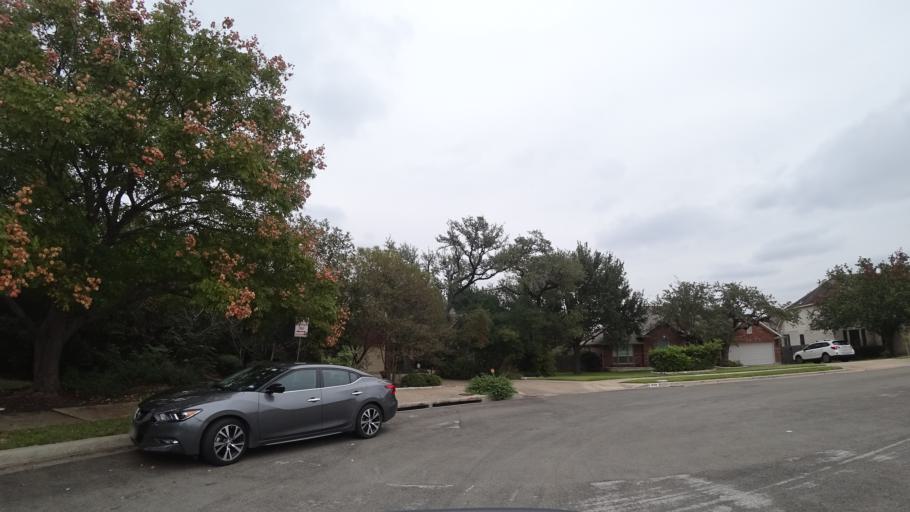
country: US
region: Texas
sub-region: Travis County
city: Shady Hollow
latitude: 30.2095
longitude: -97.8786
